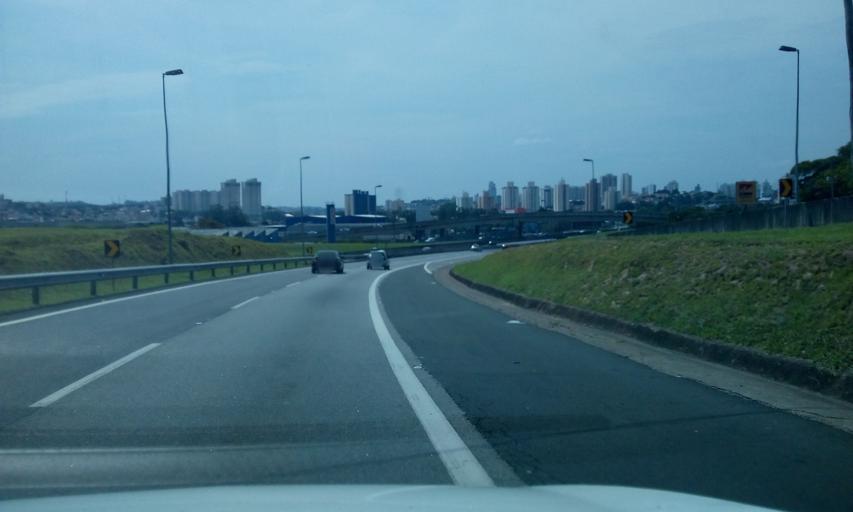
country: BR
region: Sao Paulo
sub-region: Jundiai
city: Jundiai
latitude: -23.1725
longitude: -46.9234
